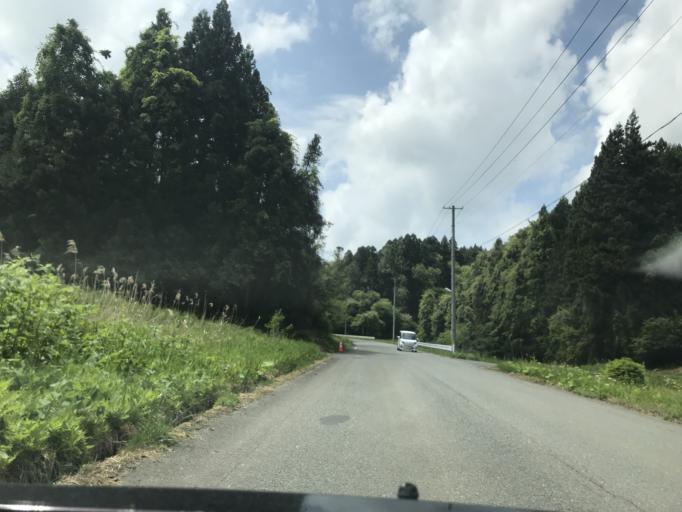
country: JP
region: Miyagi
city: Furukawa
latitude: 38.7371
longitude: 140.9289
